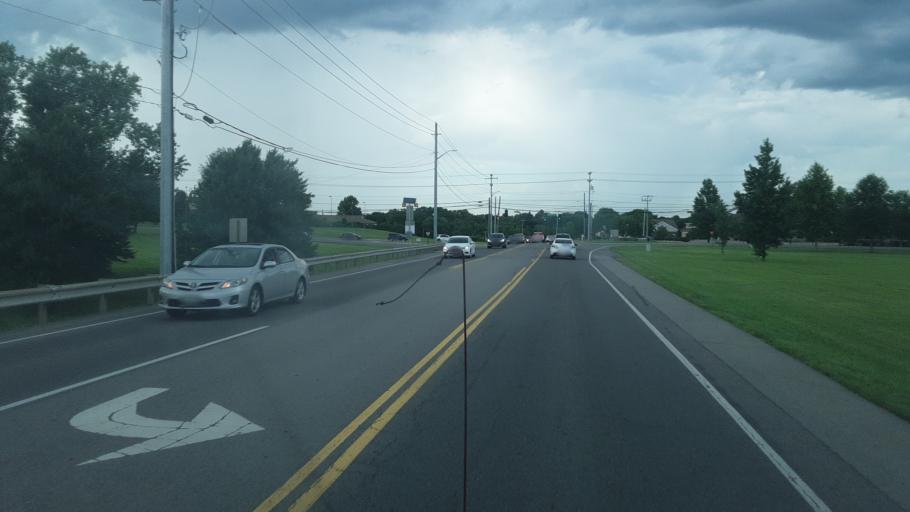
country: US
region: Tennessee
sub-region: Montgomery County
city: Clarksville
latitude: 36.5199
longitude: -87.2779
